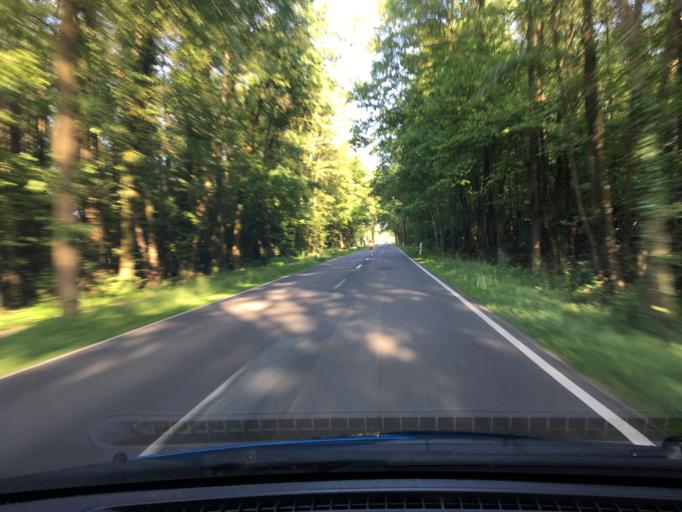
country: DE
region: Lower Saxony
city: Otter
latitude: 53.2555
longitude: 9.7515
